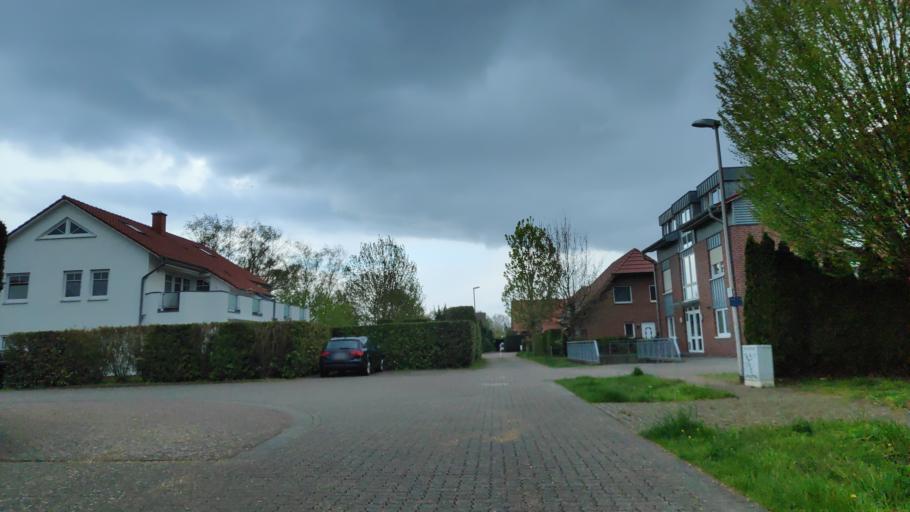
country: DE
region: North Rhine-Westphalia
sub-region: Regierungsbezirk Detmold
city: Minden
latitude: 52.3135
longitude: 8.9098
